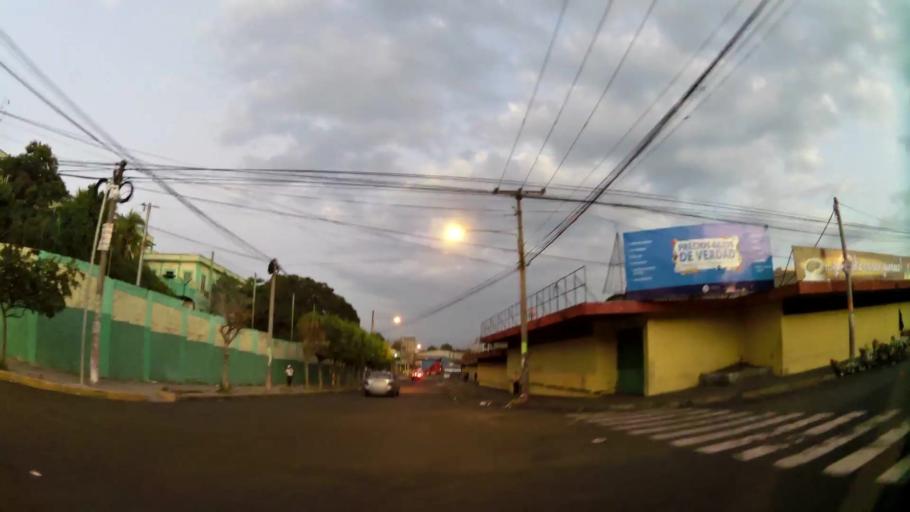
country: SV
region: San Salvador
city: San Salvador
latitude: 13.7091
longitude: -89.1904
